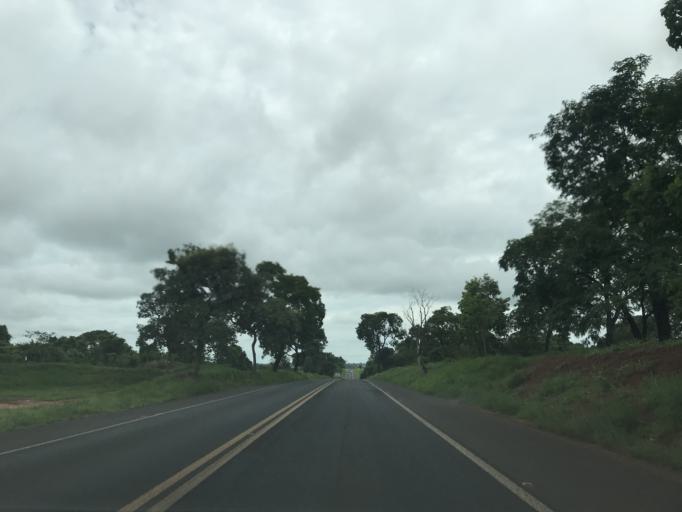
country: BR
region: Sao Paulo
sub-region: Nova Granada
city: Nova Granada
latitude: -20.4338
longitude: -49.2762
